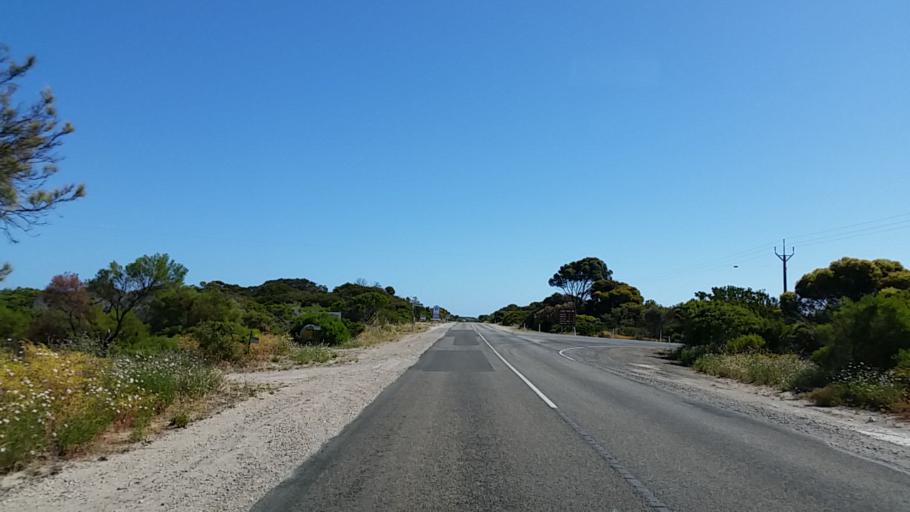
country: AU
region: South Australia
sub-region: Yorke Peninsula
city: Honiton
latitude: -35.2332
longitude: 136.9821
